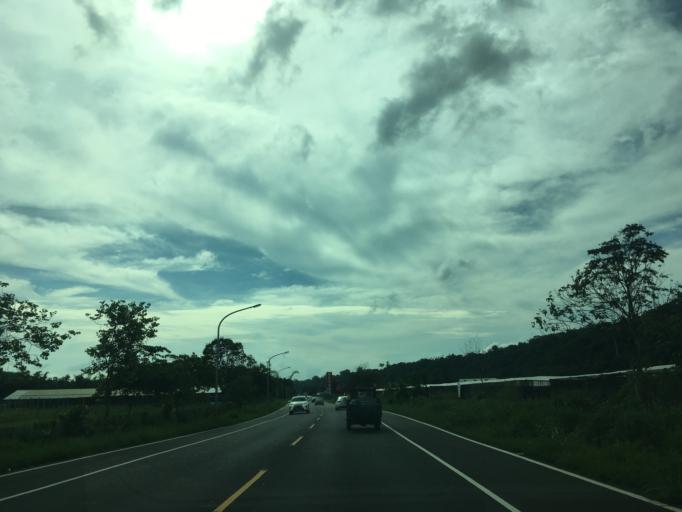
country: TW
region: Taiwan
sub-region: Chiayi
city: Jiayi Shi
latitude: 23.4471
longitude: 120.5803
